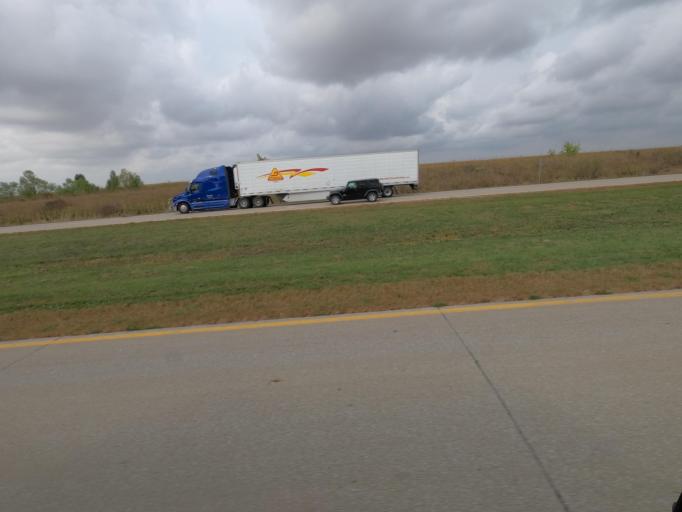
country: US
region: Iowa
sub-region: Wapello County
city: Ottumwa
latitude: 41.0039
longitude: -92.2926
